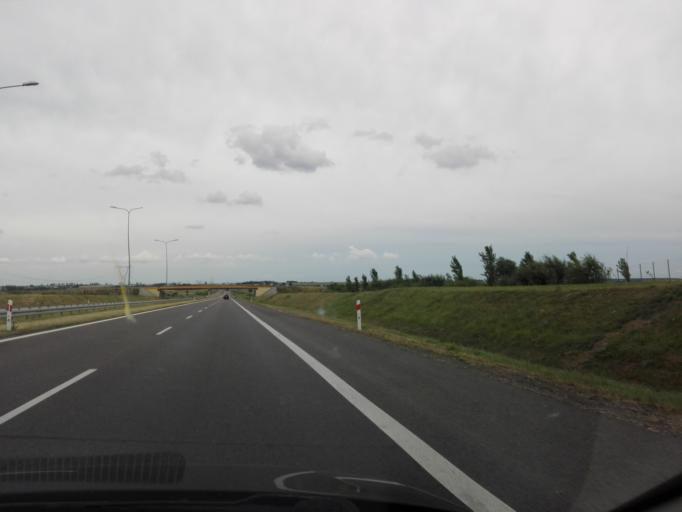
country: PL
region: Lublin Voivodeship
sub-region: Powiat pulawski
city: Markuszow
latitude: 51.3877
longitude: 22.2559
